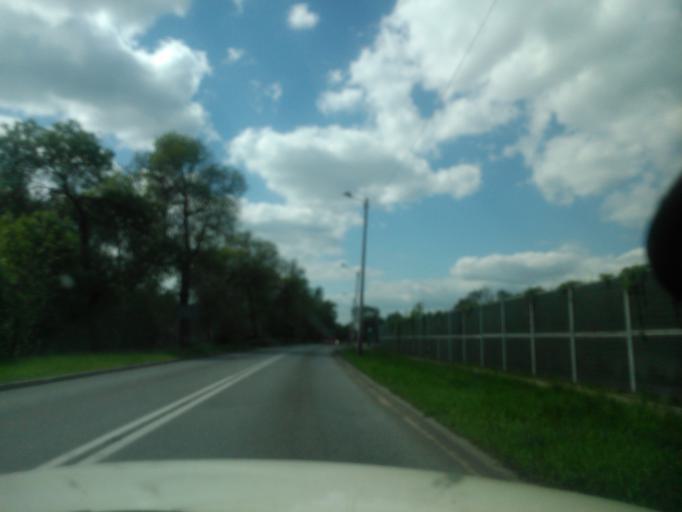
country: PL
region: Swietokrzyskie
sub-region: Powiat ostrowiecki
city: Kunow
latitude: 50.9617
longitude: 21.2801
